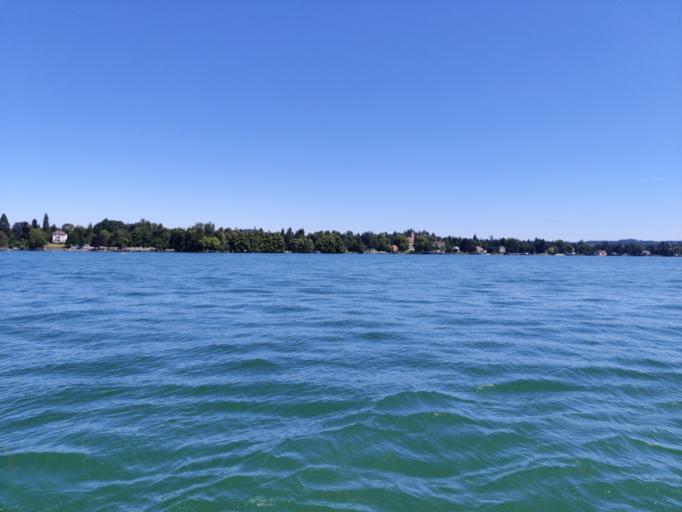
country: DE
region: Bavaria
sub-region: Swabia
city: Bodolz
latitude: 47.5507
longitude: 9.6569
